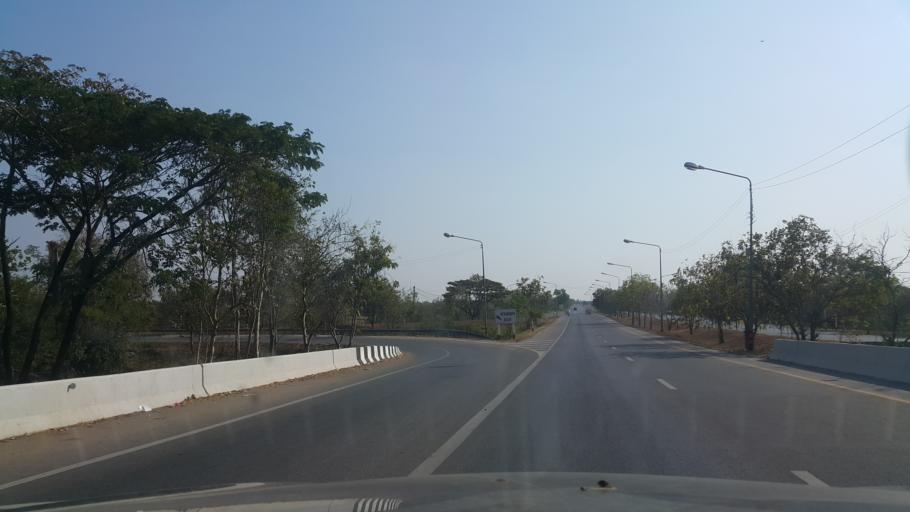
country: TH
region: Khon Kaen
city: Khon Kaen
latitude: 16.4358
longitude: 102.9179
